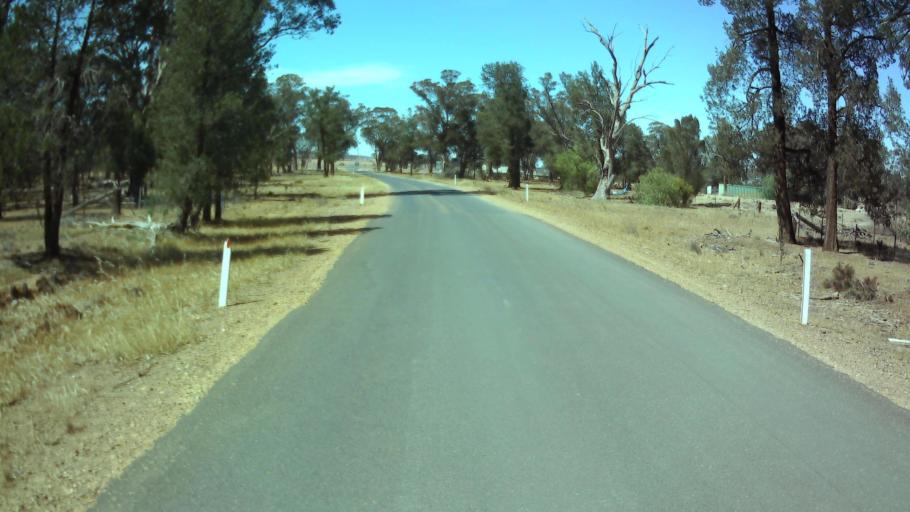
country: AU
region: New South Wales
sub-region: Weddin
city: Grenfell
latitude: -34.1172
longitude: 147.8844
